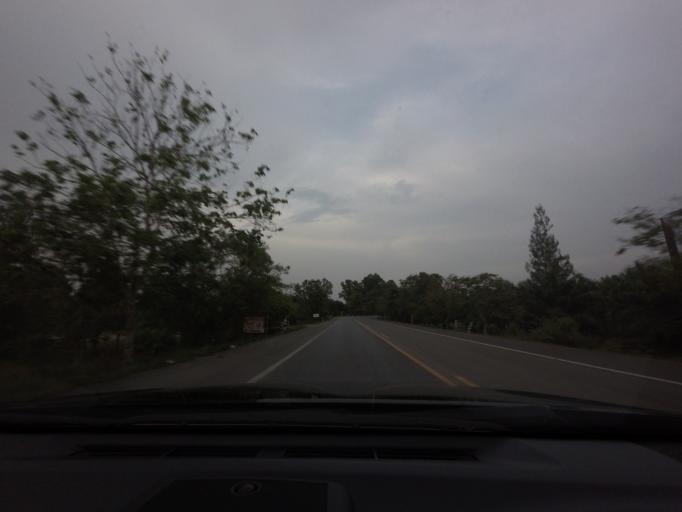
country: TH
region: Surat Thani
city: Phunphin
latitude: 9.1522
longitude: 99.1575
